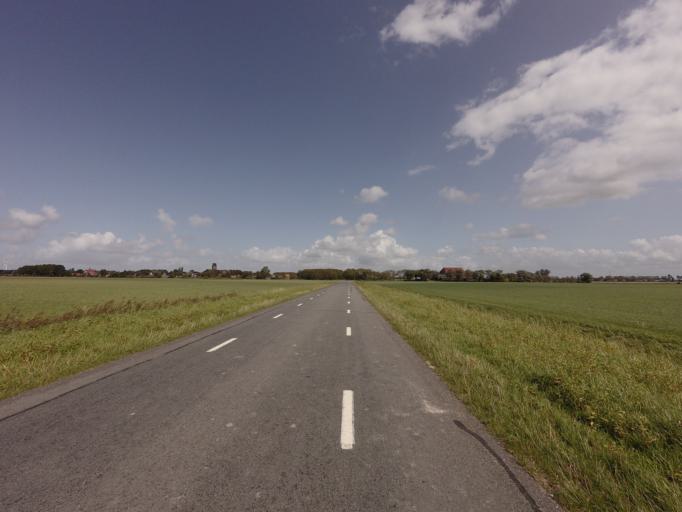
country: NL
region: Friesland
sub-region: Sudwest Fryslan
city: Makkum
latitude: 53.1101
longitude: 5.4374
